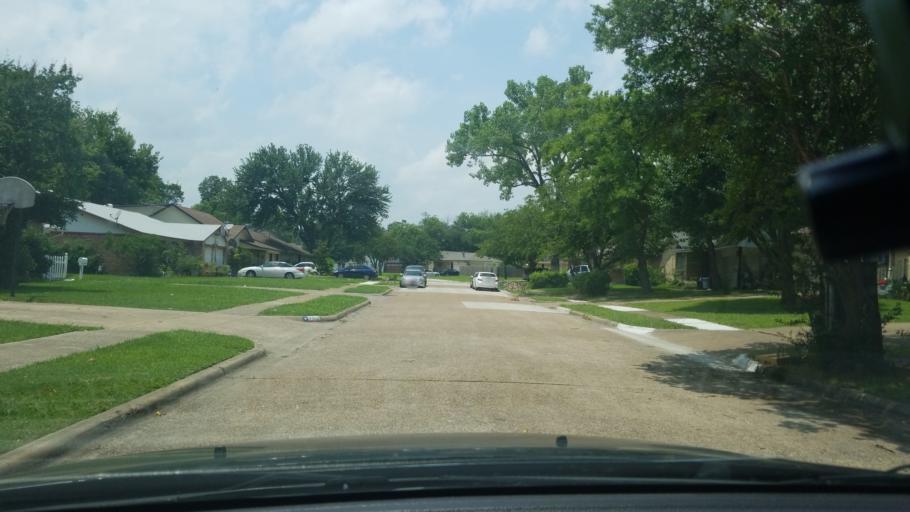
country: US
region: Texas
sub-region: Dallas County
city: Mesquite
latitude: 32.7942
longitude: -96.6427
